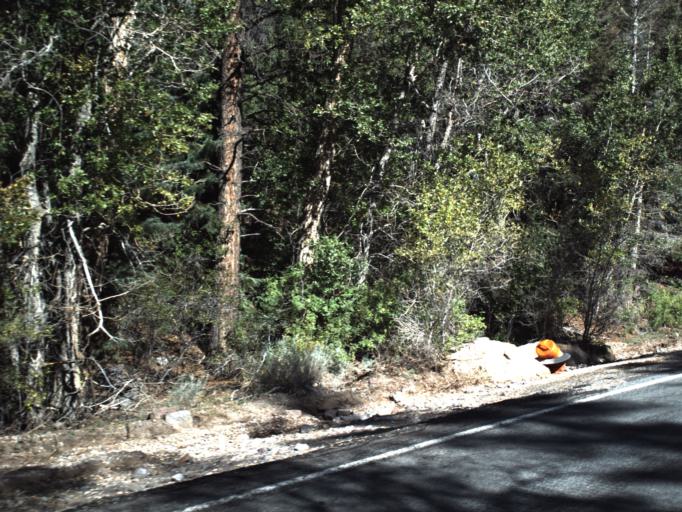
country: US
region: Utah
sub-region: Iron County
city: Parowan
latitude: 37.7564
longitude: -112.8418
